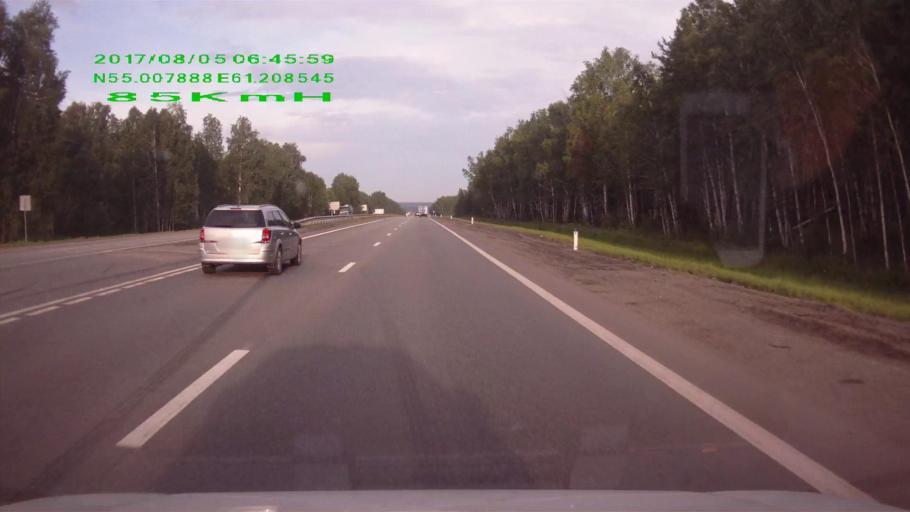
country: RU
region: Chelyabinsk
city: Sargazy
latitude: 55.0079
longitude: 61.2081
